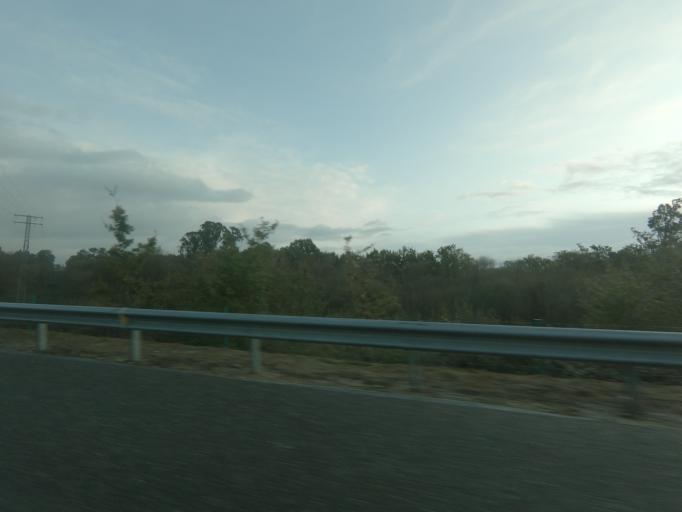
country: ES
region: Galicia
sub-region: Provincia de Pontevedra
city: Tui
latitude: 42.0878
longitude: -8.6404
